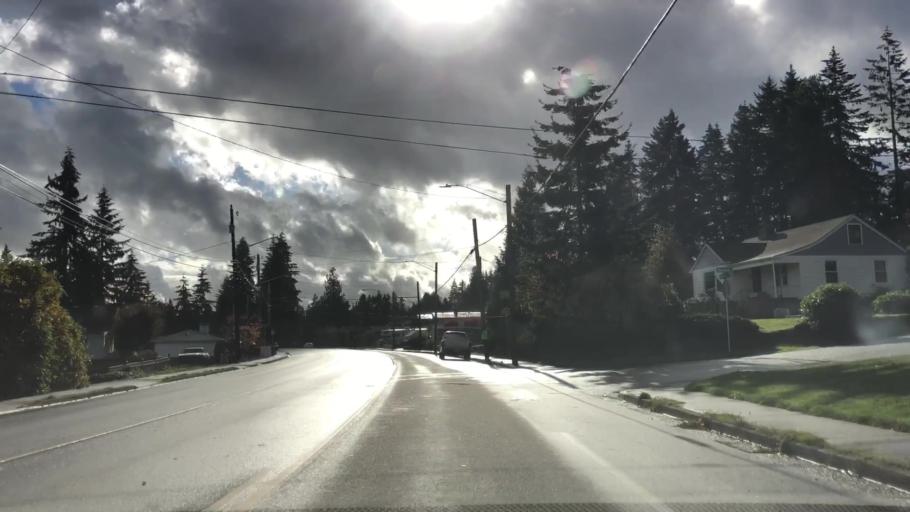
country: US
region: Washington
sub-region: Snohomish County
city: Everett
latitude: 47.9340
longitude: -122.2123
